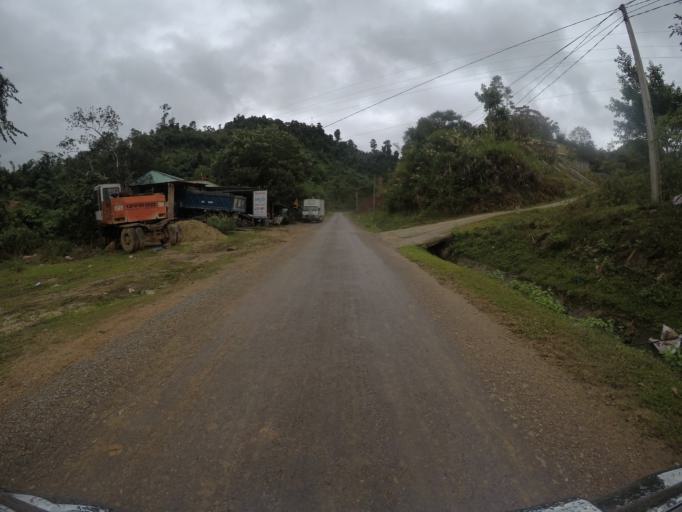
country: LA
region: Xekong
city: Dak Cheung
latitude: 15.6009
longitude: 107.4527
